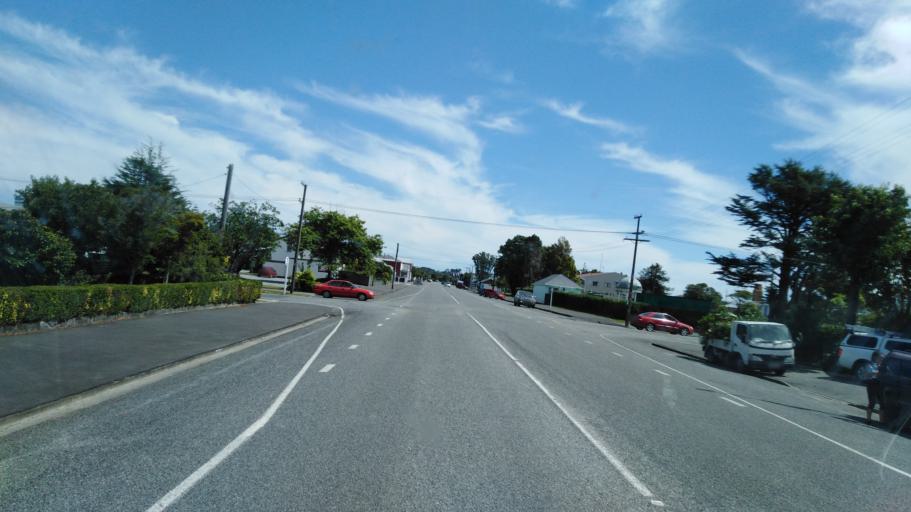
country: NZ
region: West Coast
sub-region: Buller District
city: Westport
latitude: -41.7548
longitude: 171.6036
